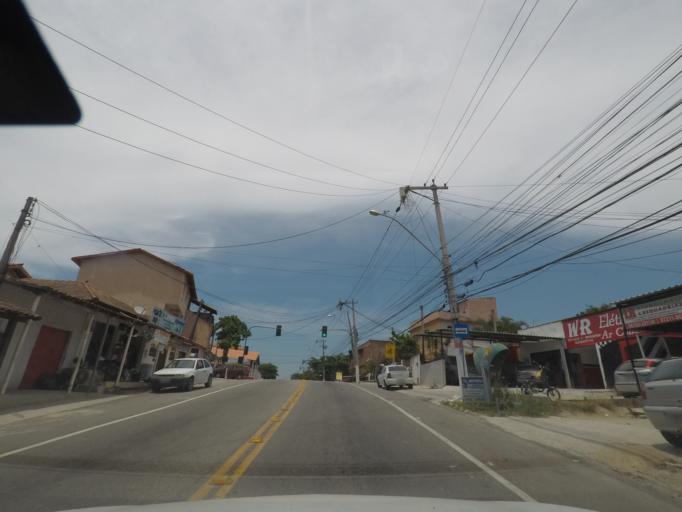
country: BR
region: Rio de Janeiro
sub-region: Marica
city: Marica
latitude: -22.9337
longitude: -42.8250
